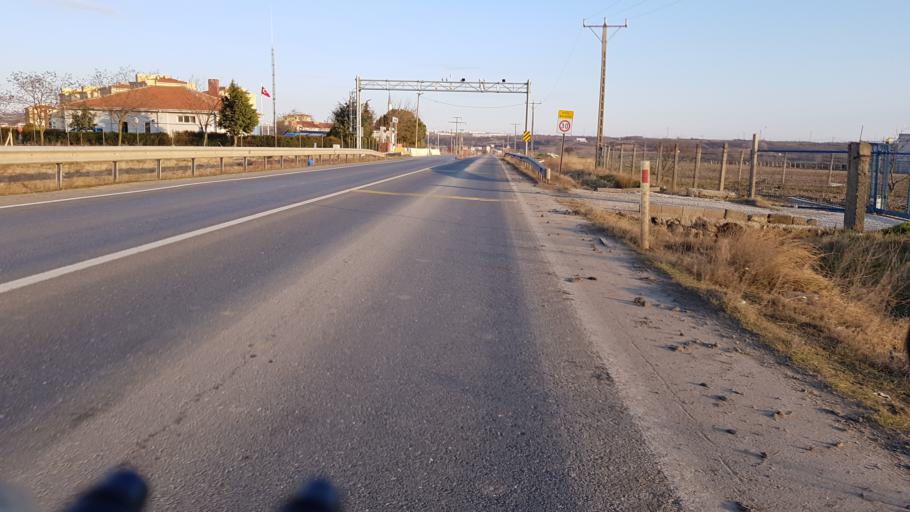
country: TR
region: Tekirdag
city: Velimese
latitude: 41.2545
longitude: 27.8631
